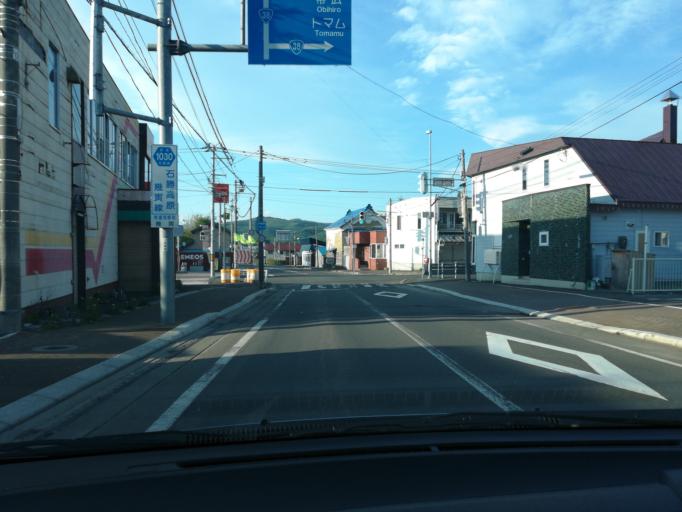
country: JP
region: Hokkaido
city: Shimo-furano
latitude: 43.1630
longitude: 142.5682
